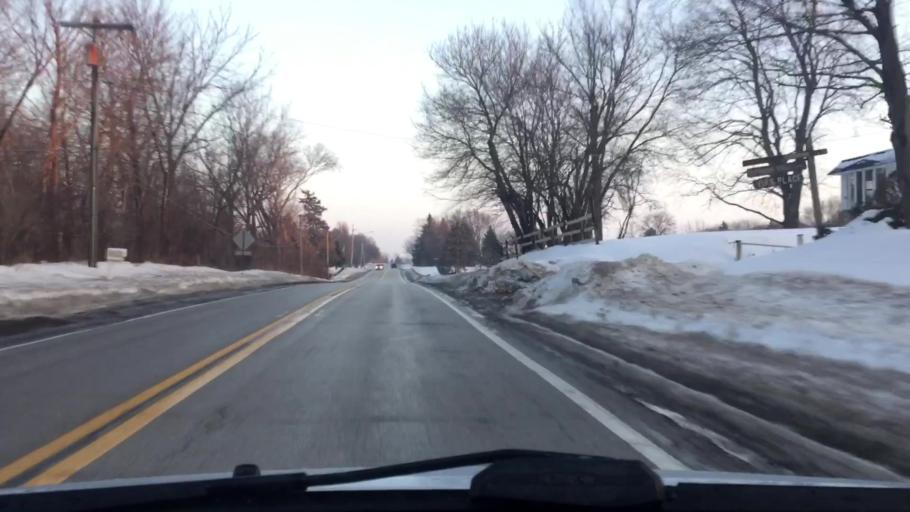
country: US
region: Illinois
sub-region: Kane County
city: Wasco
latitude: 41.9482
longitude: -88.4057
